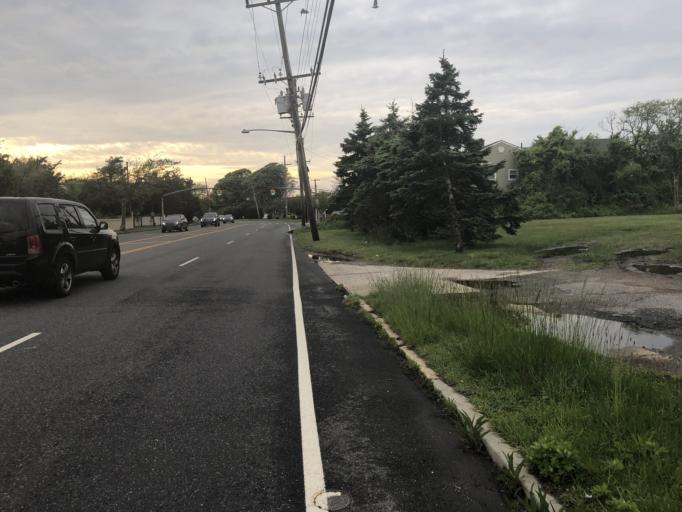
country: US
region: New York
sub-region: Nassau County
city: Atlantic Beach
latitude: 40.5877
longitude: -73.7185
